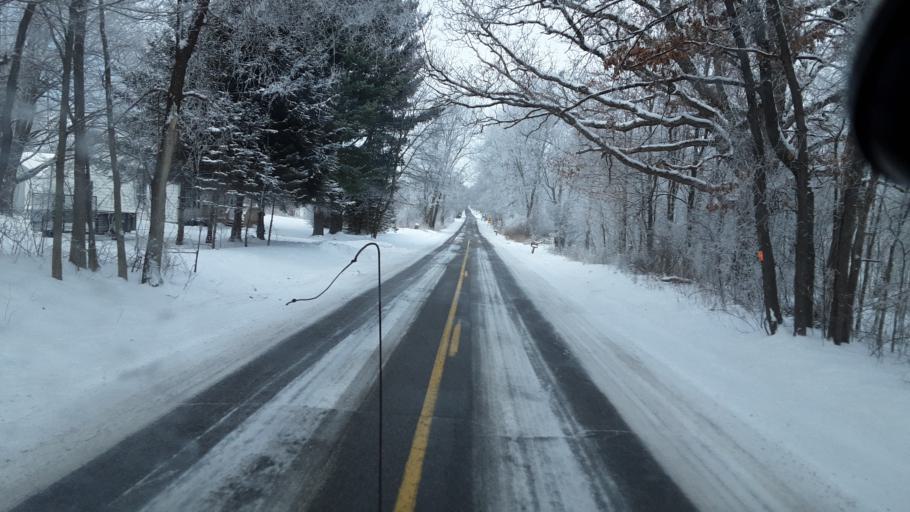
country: US
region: Michigan
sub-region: Eaton County
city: Eaton Rapids
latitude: 42.4657
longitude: -84.5561
